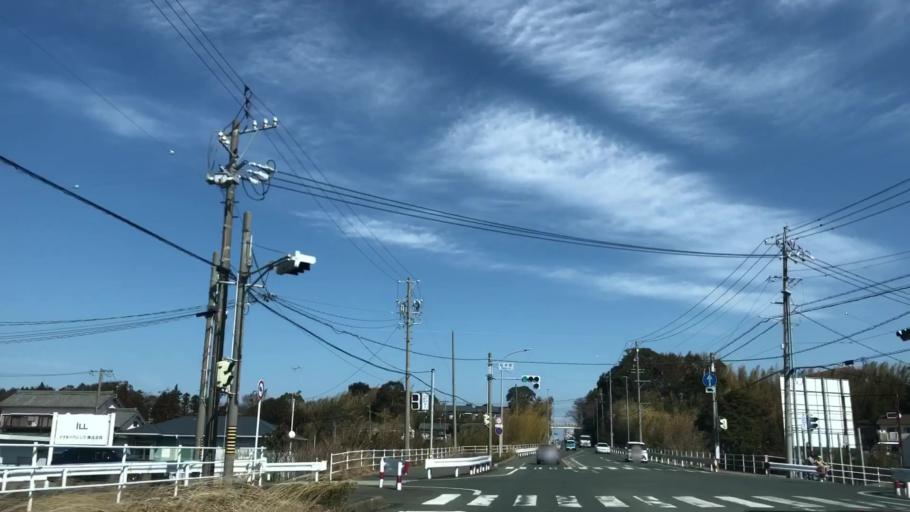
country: JP
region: Aichi
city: Toyohashi
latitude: 34.7208
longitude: 137.3714
